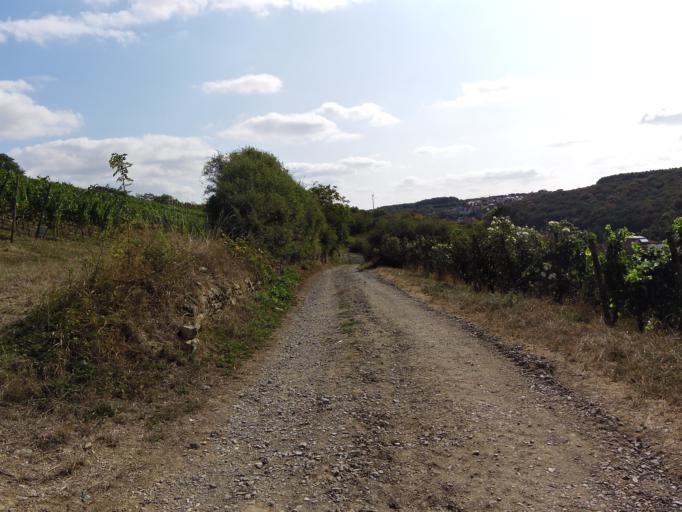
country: DE
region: Bavaria
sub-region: Regierungsbezirk Unterfranken
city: Theilheim
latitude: 49.7553
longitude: 10.0130
